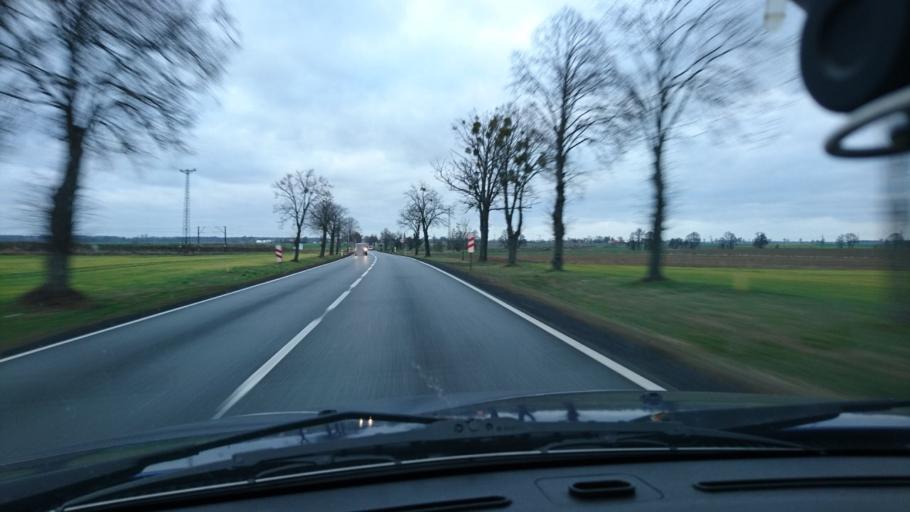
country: PL
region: Opole Voivodeship
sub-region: Powiat kluczborski
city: Kluczbork
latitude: 51.0141
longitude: 18.2013
